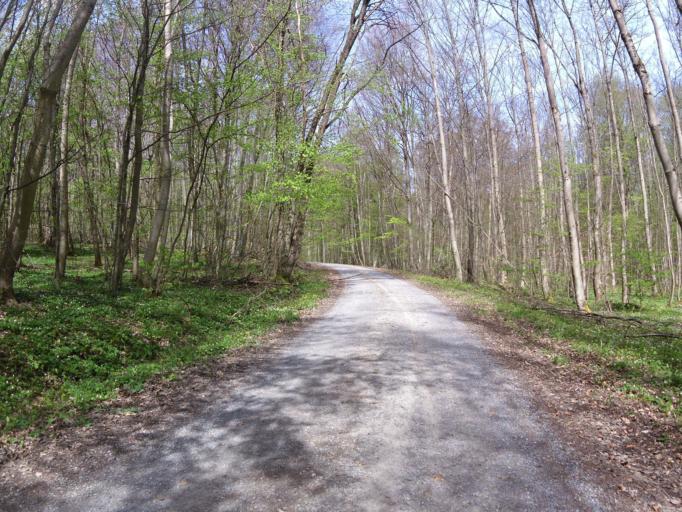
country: DE
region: Bavaria
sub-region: Regierungsbezirk Unterfranken
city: Rimpar
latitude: 49.8642
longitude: 9.9884
